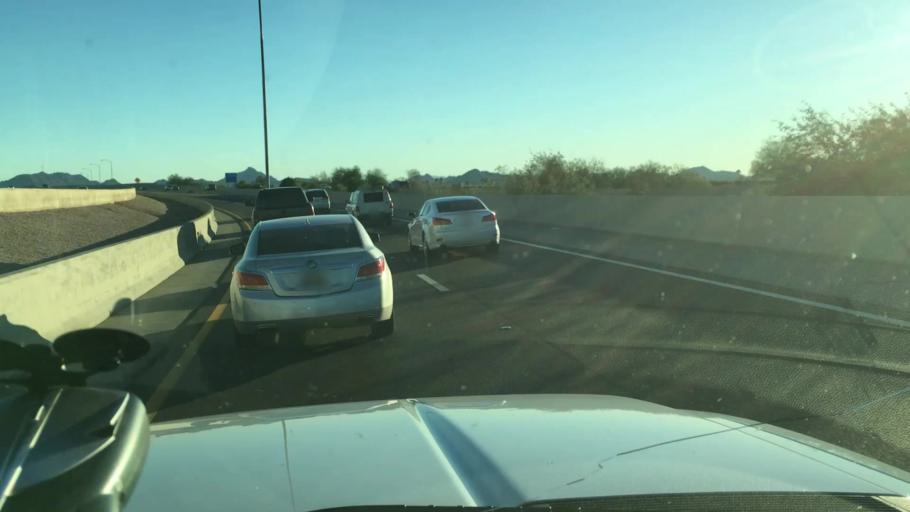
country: US
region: Arizona
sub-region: Maricopa County
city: Paradise Valley
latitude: 33.6675
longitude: -111.9974
